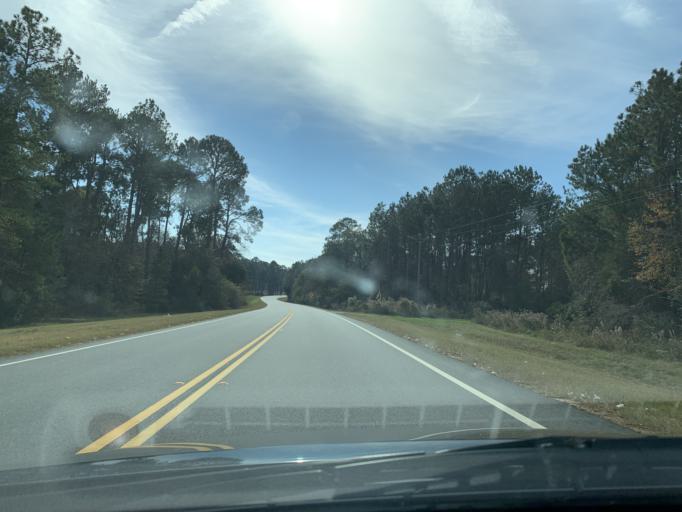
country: US
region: Georgia
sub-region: Turner County
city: Ashburn
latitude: 31.7279
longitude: -83.5812
